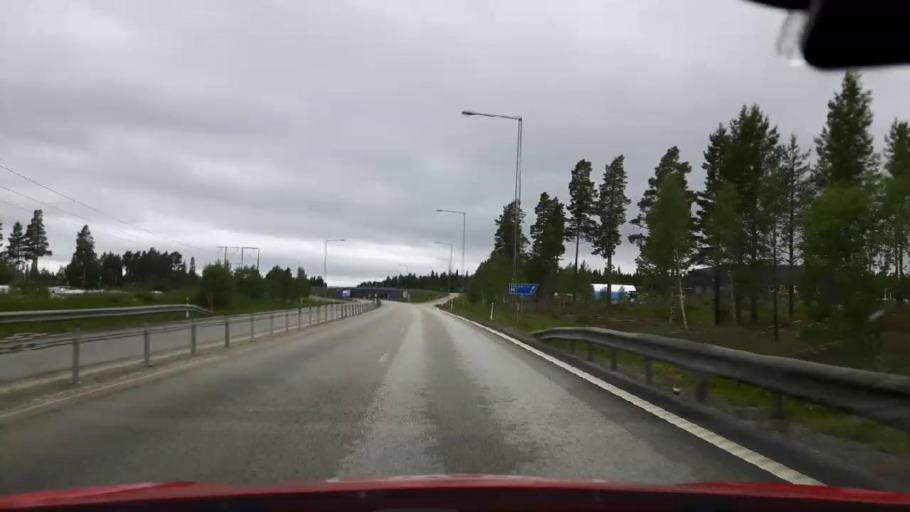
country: SE
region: Jaemtland
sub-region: OEstersunds Kommun
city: Ostersund
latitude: 63.1629
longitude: 14.7444
